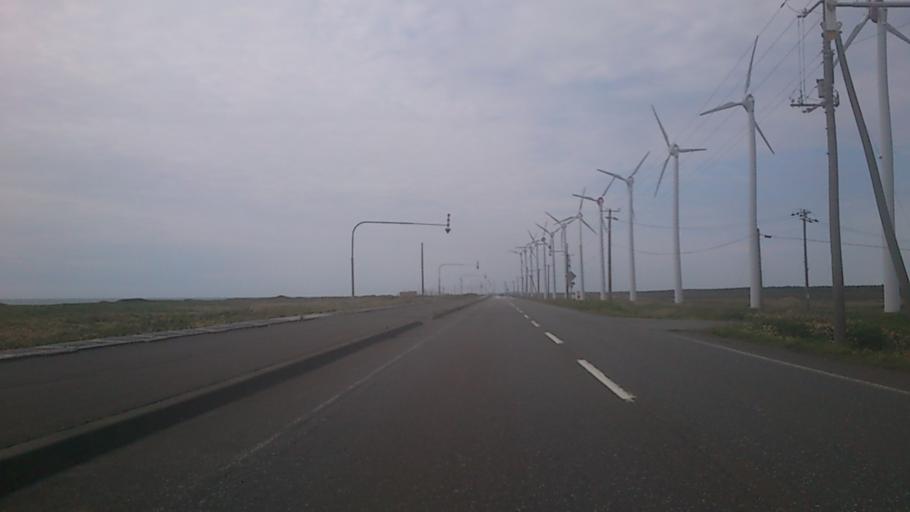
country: JP
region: Hokkaido
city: Makubetsu
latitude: 44.9694
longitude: 141.7002
